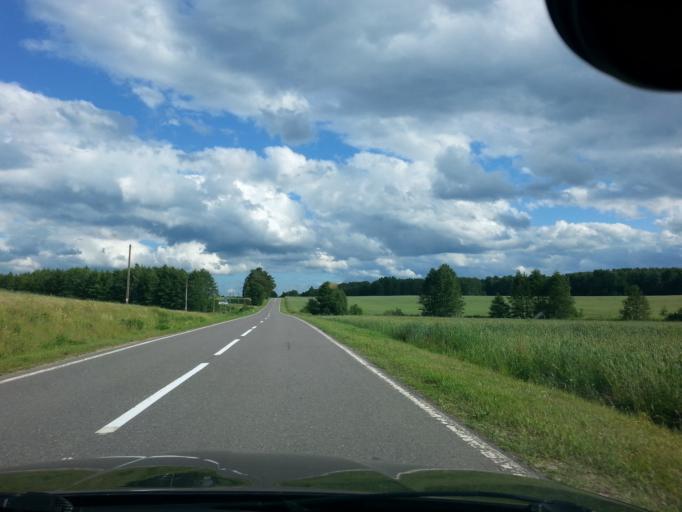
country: BY
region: Minsk
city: Svir
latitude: 54.9432
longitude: 26.3676
